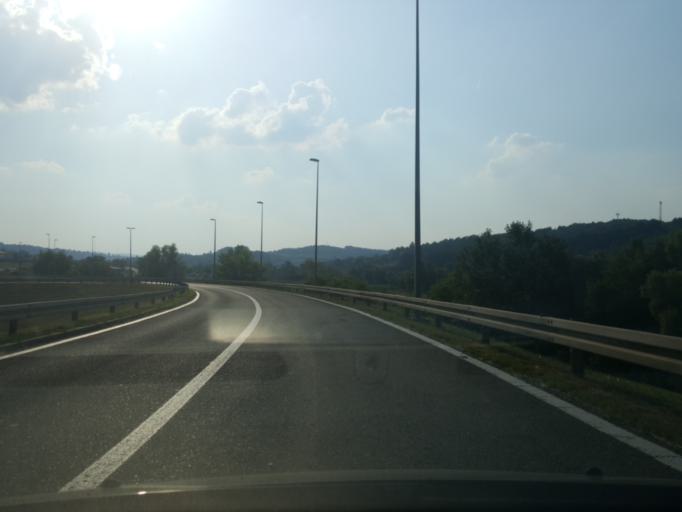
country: RS
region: Central Serbia
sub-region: Belgrade
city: Sopot
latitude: 44.5668
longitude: 20.6670
